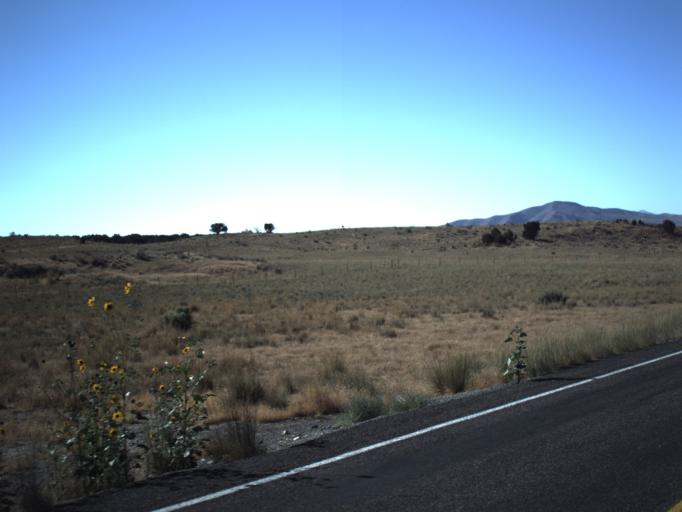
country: US
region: Utah
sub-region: Juab County
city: Mona
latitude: 39.7467
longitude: -112.1856
